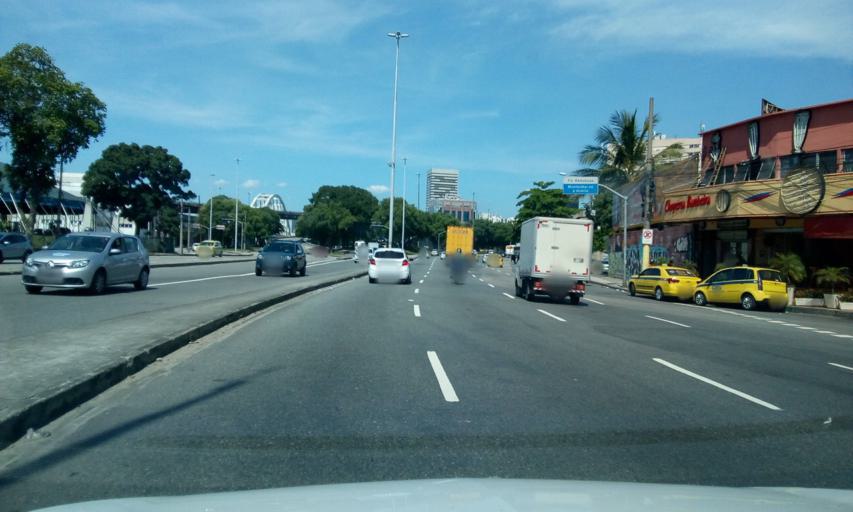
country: BR
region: Rio de Janeiro
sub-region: Rio De Janeiro
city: Rio de Janeiro
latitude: -22.9111
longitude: -43.2137
